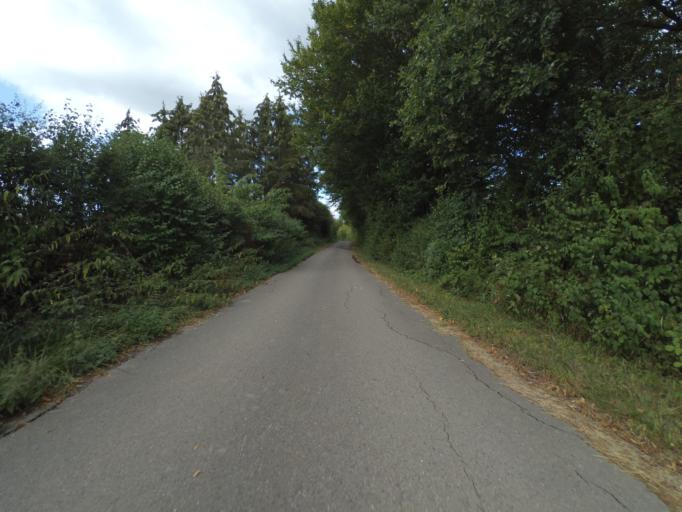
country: LU
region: Grevenmacher
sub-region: Canton de Remich
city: Lenningen
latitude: 49.6084
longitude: 6.3772
